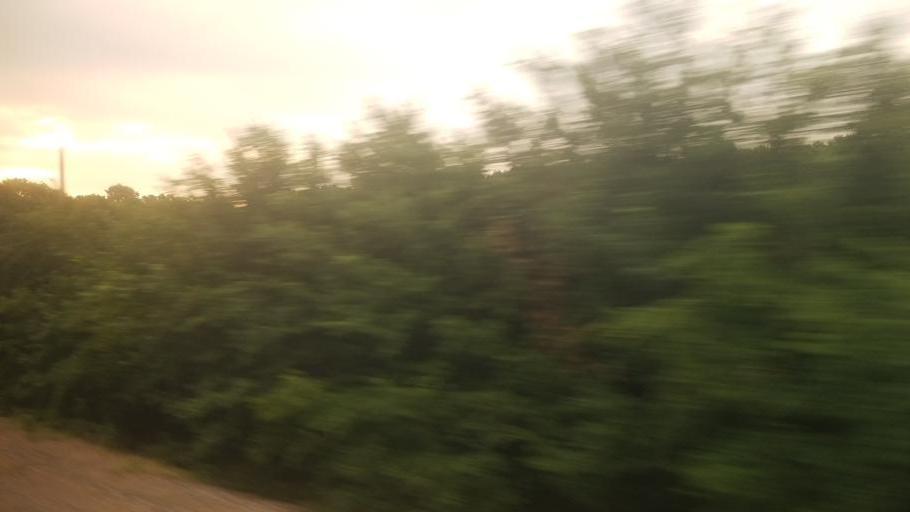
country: US
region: Kansas
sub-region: Chase County
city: Cottonwood Falls
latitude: 38.3931
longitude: -96.6263
